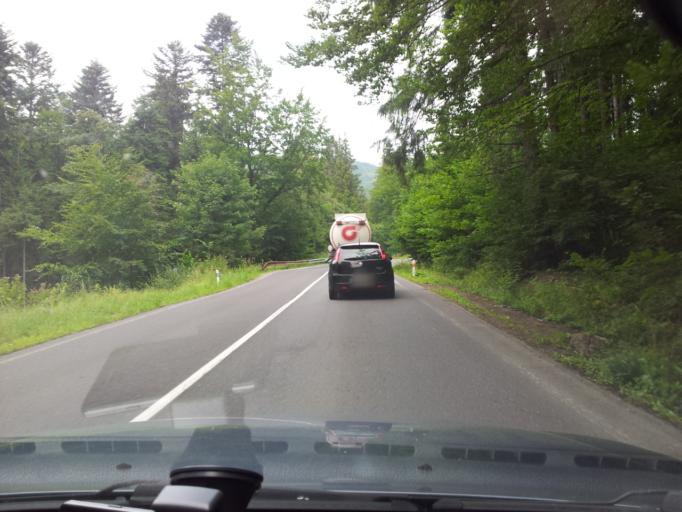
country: SK
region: Zilinsky
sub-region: Okres Dolny Kubin
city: Dolny Kubin
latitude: 49.2920
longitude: 19.3489
